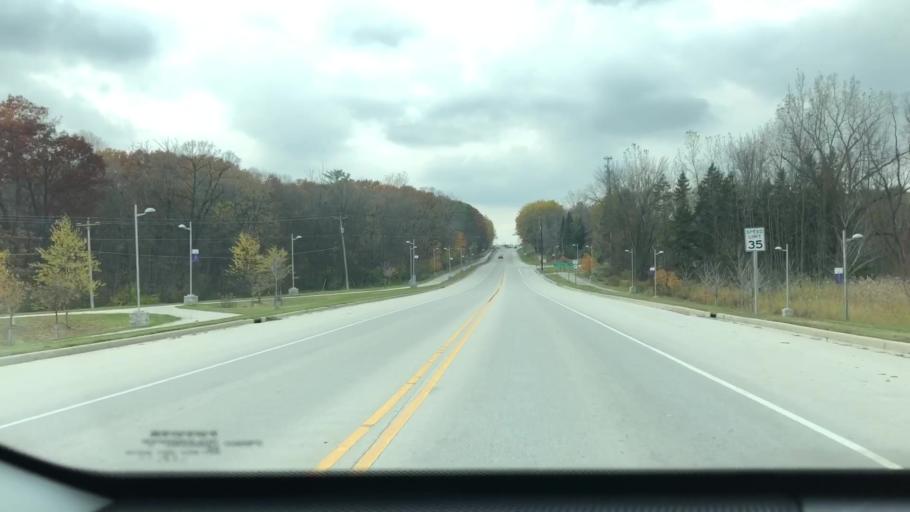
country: US
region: Wisconsin
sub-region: Brown County
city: Oneida
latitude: 44.4995
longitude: -88.1846
